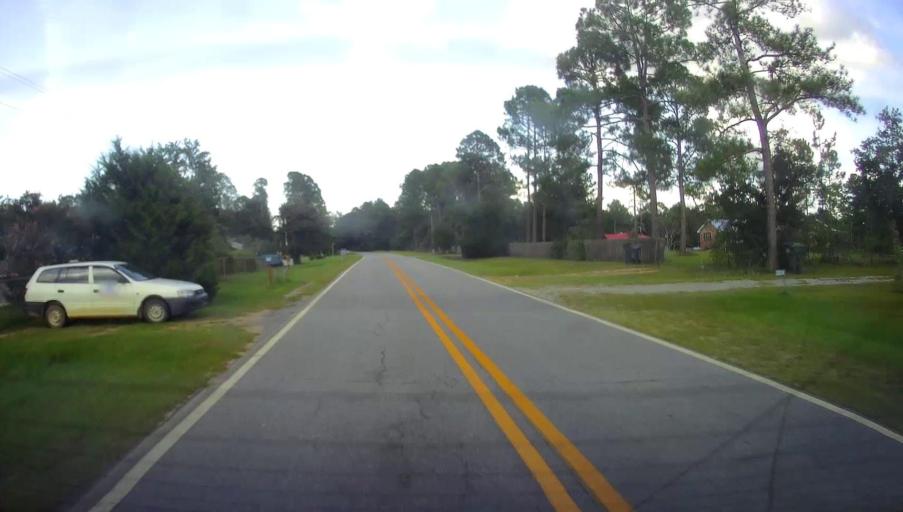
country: US
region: Georgia
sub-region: Crawford County
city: Knoxville
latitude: 32.7529
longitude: -83.9066
